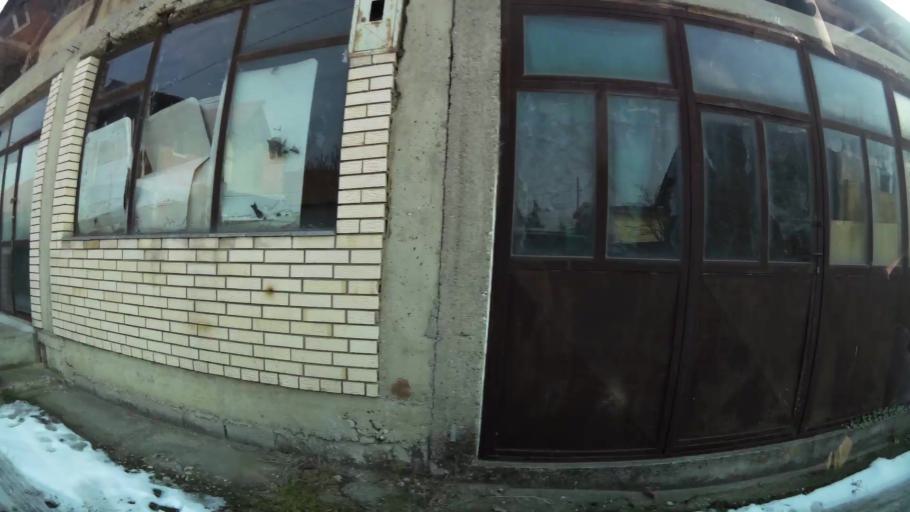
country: MK
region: Kisela Voda
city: Kisela Voda
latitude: 41.9904
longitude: 21.4975
